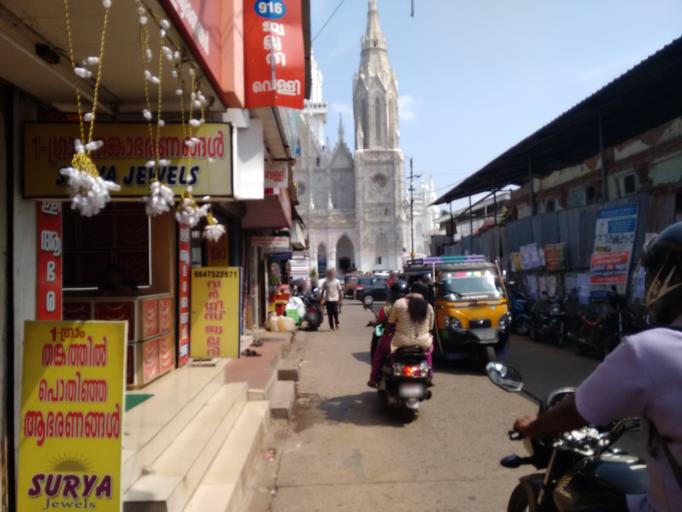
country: IN
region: Kerala
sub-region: Thrissur District
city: Trichur
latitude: 10.5209
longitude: 76.2171
